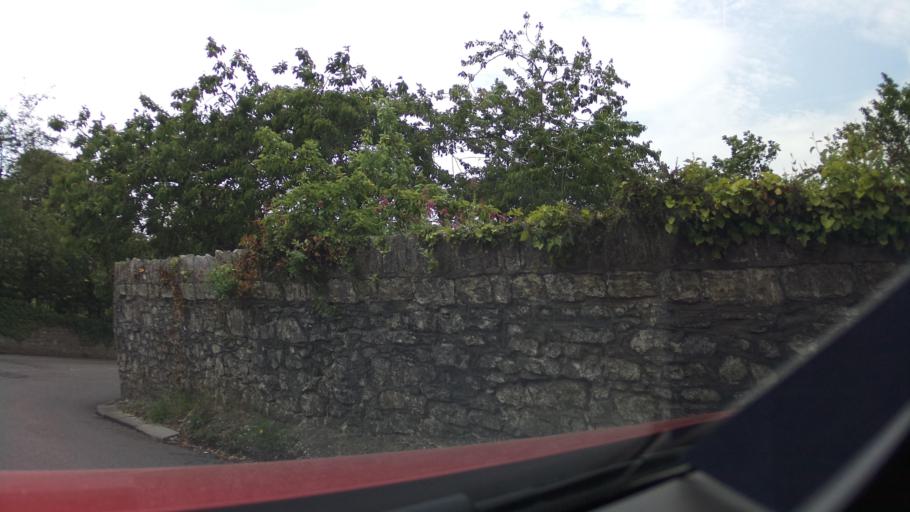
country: GB
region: Wales
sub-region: Vale of Glamorgan
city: Llantwit Major
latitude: 51.4062
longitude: -3.4630
